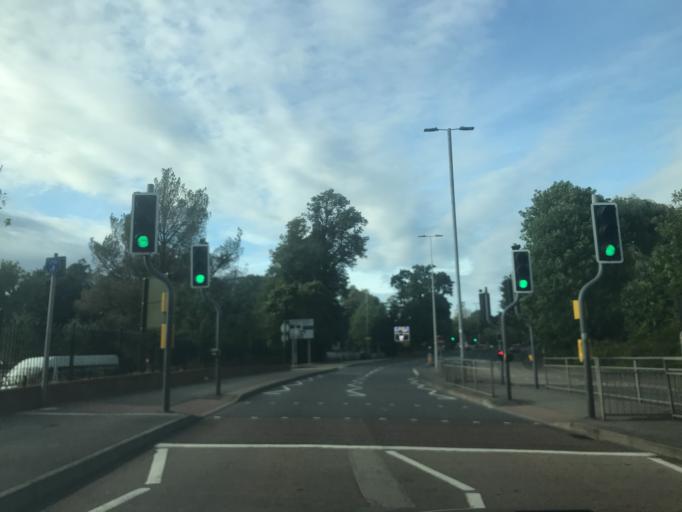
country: GB
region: England
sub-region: Bracknell Forest
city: Bracknell
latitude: 51.4111
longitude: -0.7510
